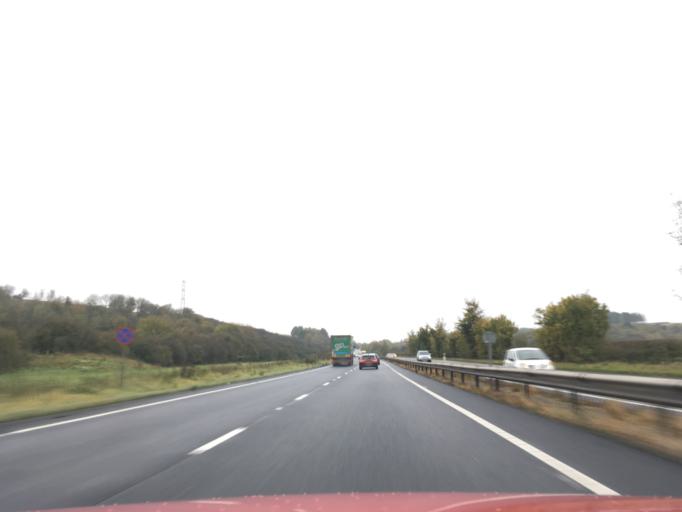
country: GB
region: England
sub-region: Hampshire
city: Highclere
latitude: 51.2990
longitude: -1.3370
